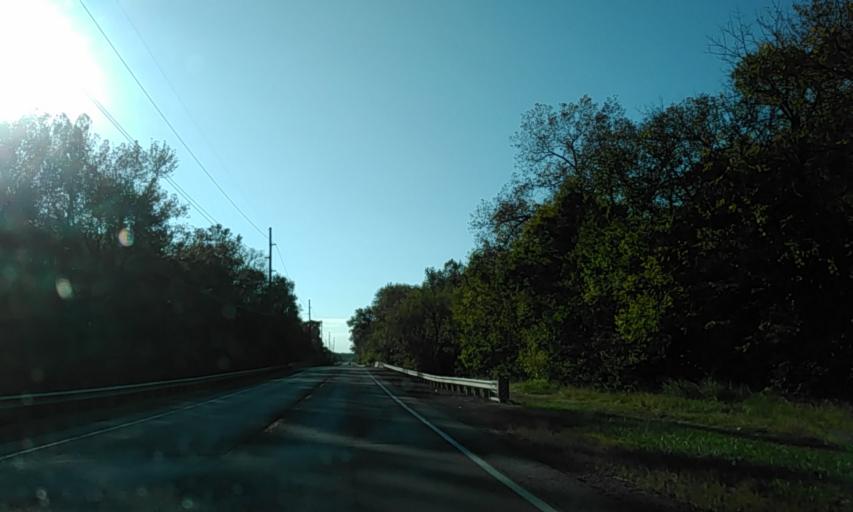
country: US
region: Illinois
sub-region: Madison County
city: Saint Jacob
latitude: 38.7161
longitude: -89.8066
